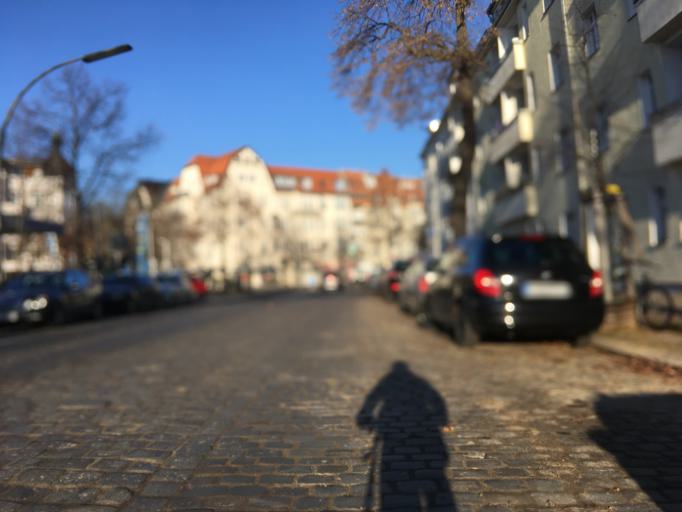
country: DE
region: Berlin
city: Steglitz Bezirk
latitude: 52.4528
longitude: 13.3156
